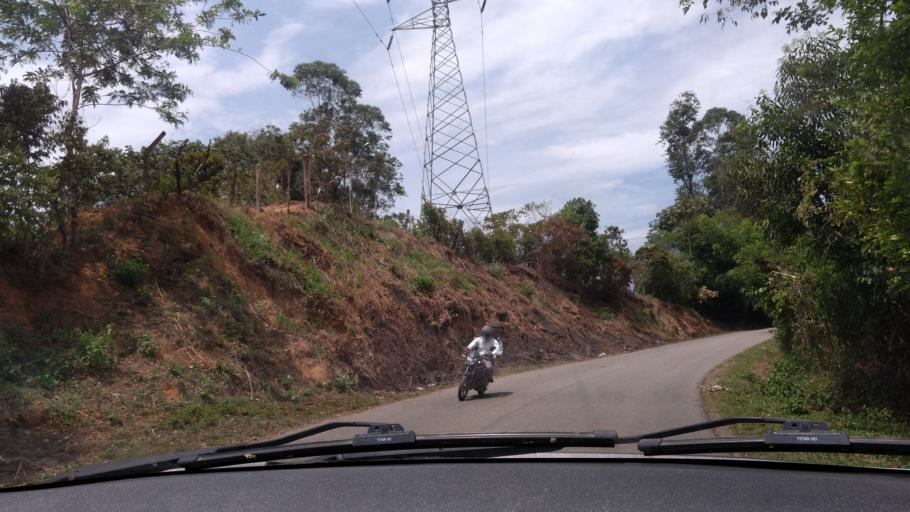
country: CO
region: Cauca
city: Buenos Aires
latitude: 3.0650
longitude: -76.6580
